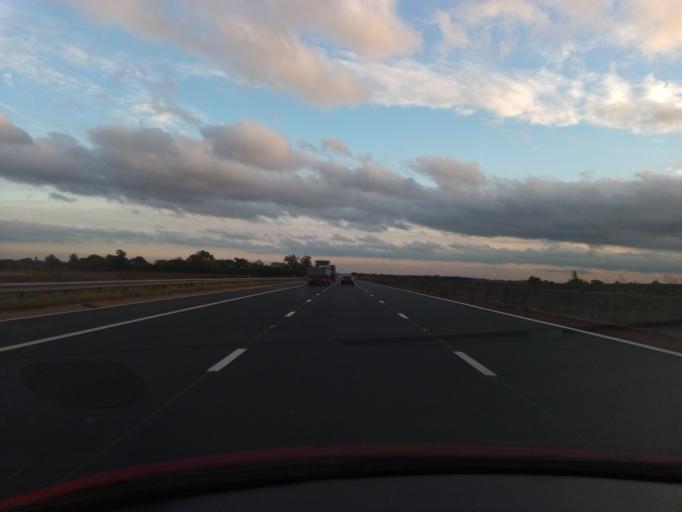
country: GB
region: England
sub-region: North Yorkshire
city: Ripon
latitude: 54.2107
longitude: -1.4774
